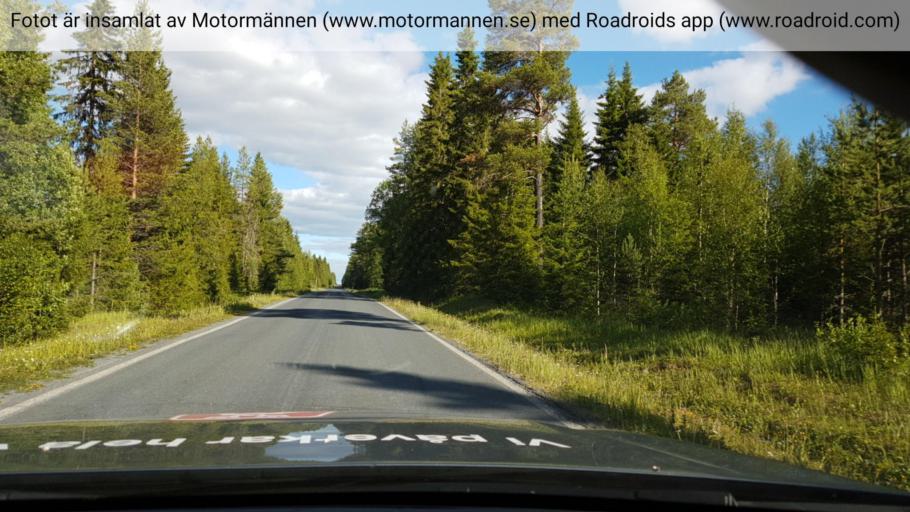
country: SE
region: Jaemtland
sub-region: Krokoms Kommun
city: Valla
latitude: 63.2960
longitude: 13.8457
